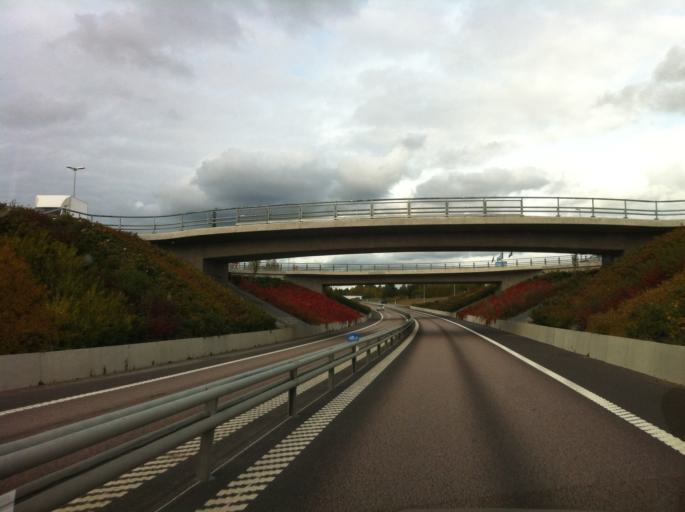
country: SE
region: OEstergoetland
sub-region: Motala Kommun
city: Motala
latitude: 58.5531
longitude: 15.0134
